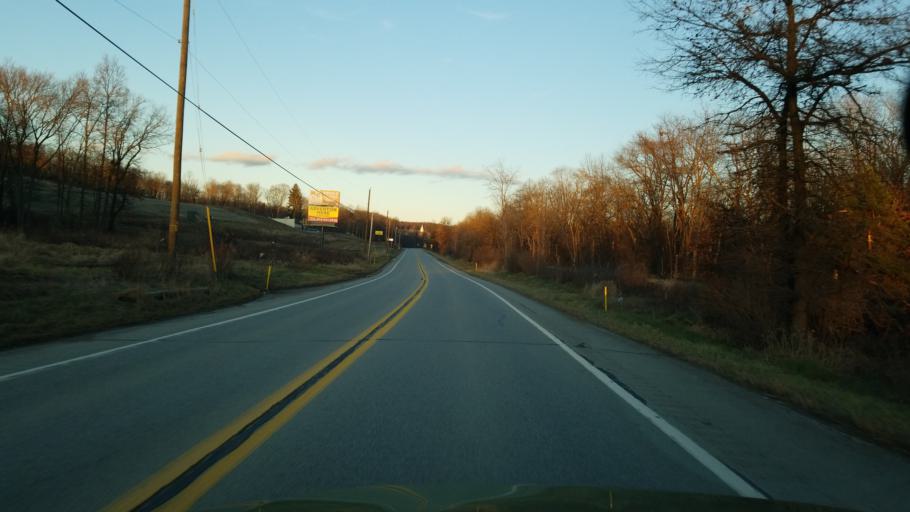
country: US
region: Pennsylvania
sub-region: Indiana County
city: Clymer
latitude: 40.7624
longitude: -79.0614
